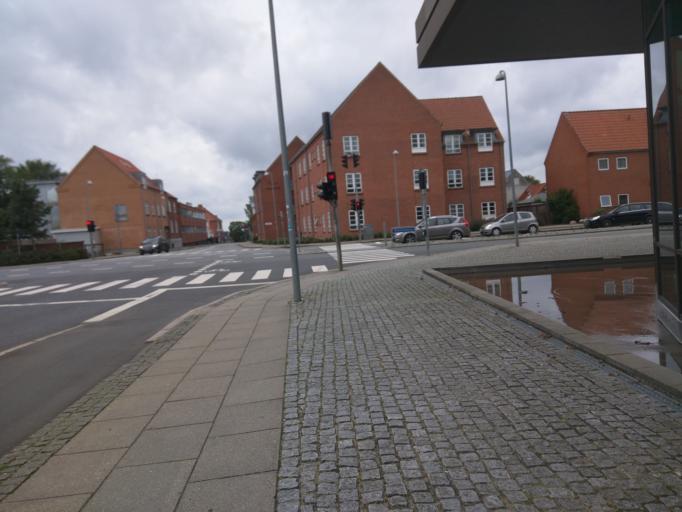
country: DK
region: Central Jutland
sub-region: Viborg Kommune
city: Viborg
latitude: 56.4534
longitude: 9.4031
